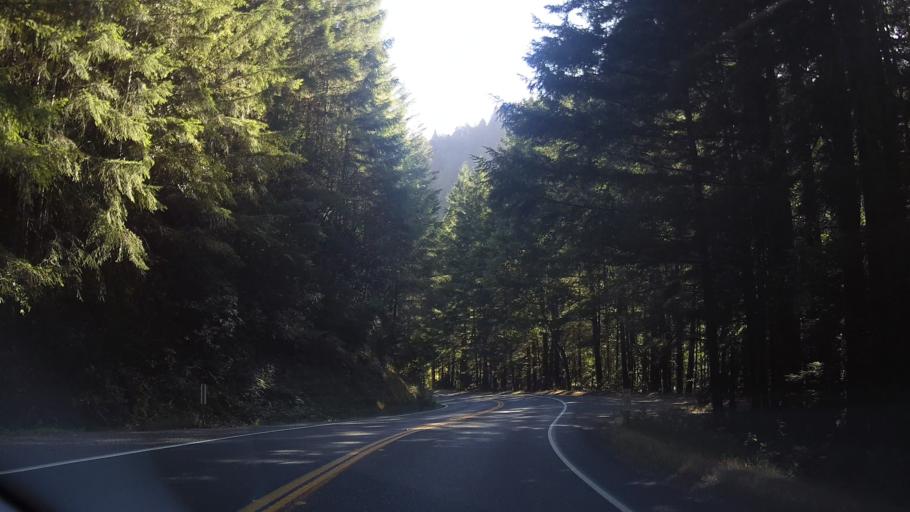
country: US
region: California
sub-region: Mendocino County
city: Brooktrails
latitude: 39.3594
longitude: -123.5085
